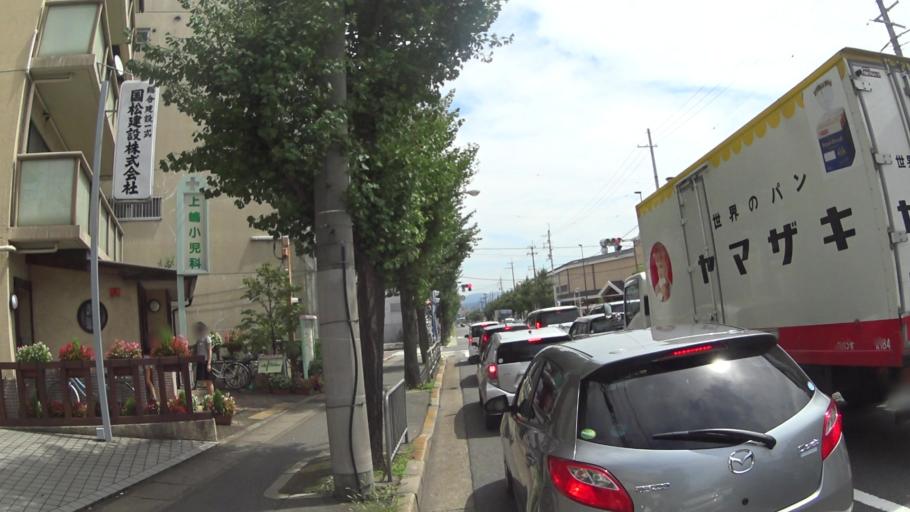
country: JP
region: Kyoto
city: Kyoto
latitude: 35.0198
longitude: 135.7087
